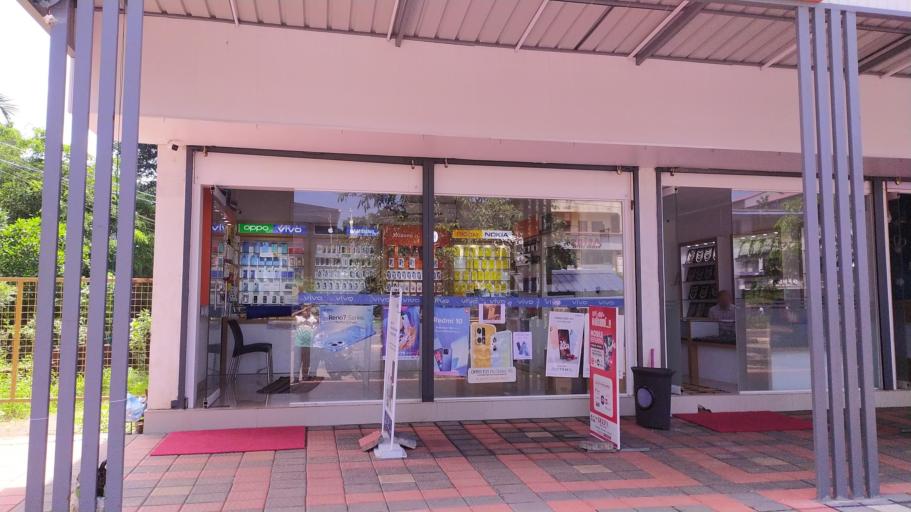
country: IN
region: Kerala
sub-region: Kasaragod District
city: Kannangad
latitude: 12.3235
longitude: 75.0859
